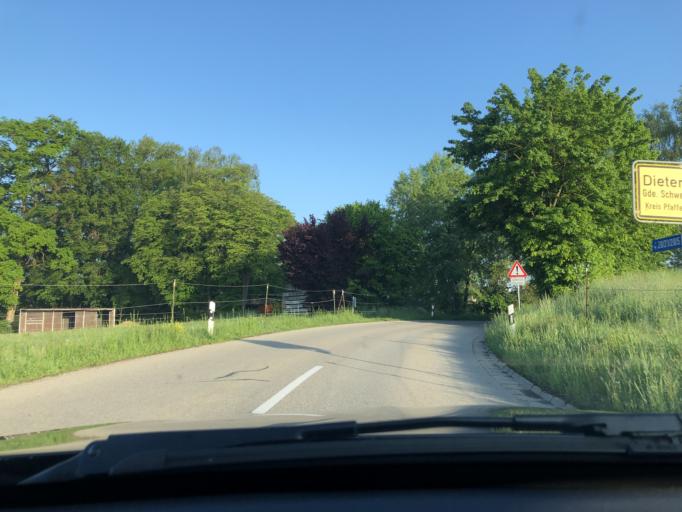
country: DE
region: Bavaria
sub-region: Upper Bavaria
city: Schweitenkirchen
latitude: 48.4878
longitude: 11.6235
